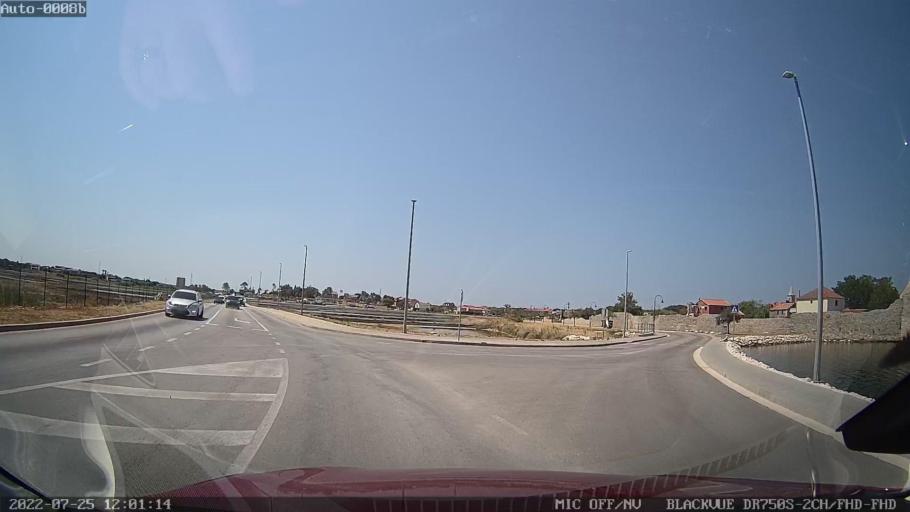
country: HR
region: Zadarska
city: Nin
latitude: 44.2430
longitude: 15.1883
